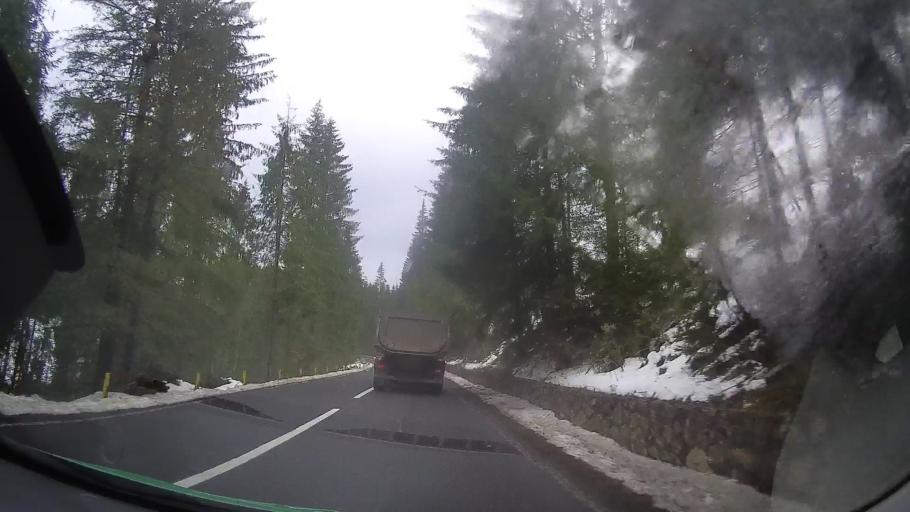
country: RO
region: Harghita
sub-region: Municipiul Gheorgheni
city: Gheorgheni
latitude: 46.7790
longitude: 25.7242
